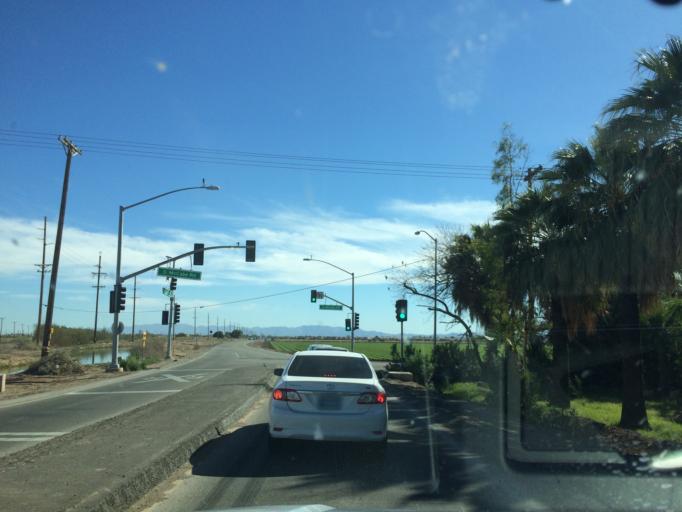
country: US
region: California
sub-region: Imperial County
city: Heber
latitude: 32.7529
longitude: -115.5349
